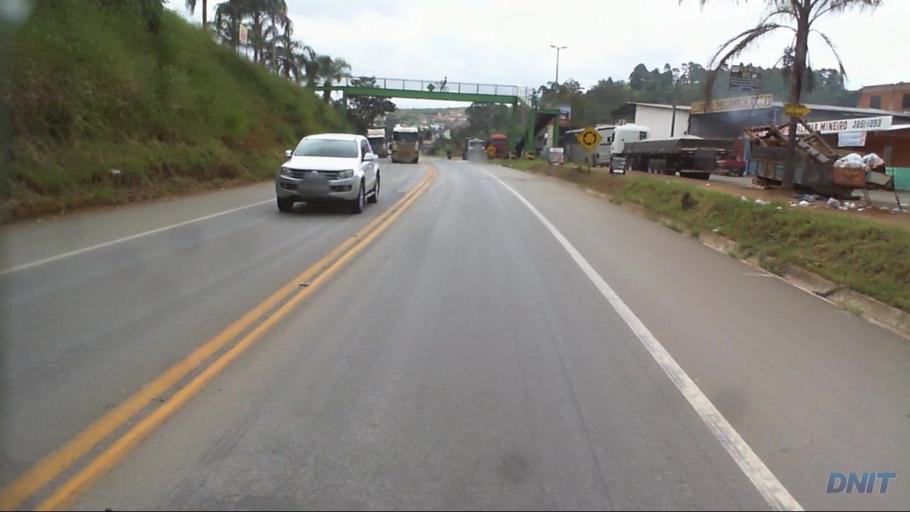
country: BR
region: Minas Gerais
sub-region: Joao Monlevade
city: Joao Monlevade
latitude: -19.8401
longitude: -43.1786
